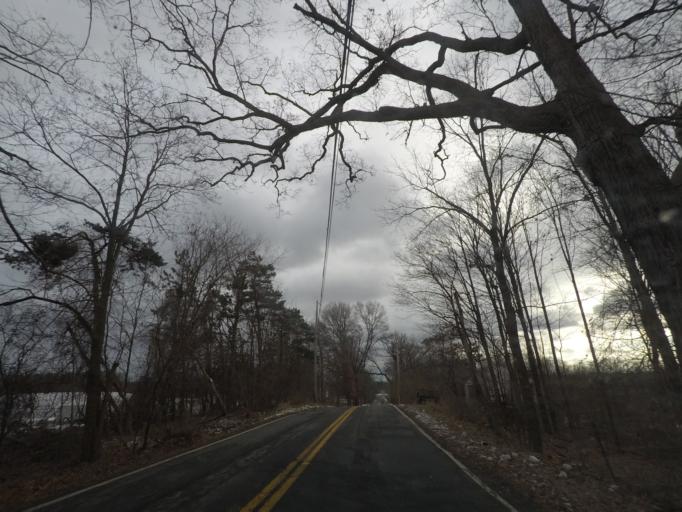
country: US
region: New York
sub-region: Rensselaer County
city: East Greenbush
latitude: 42.5877
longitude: -73.7196
